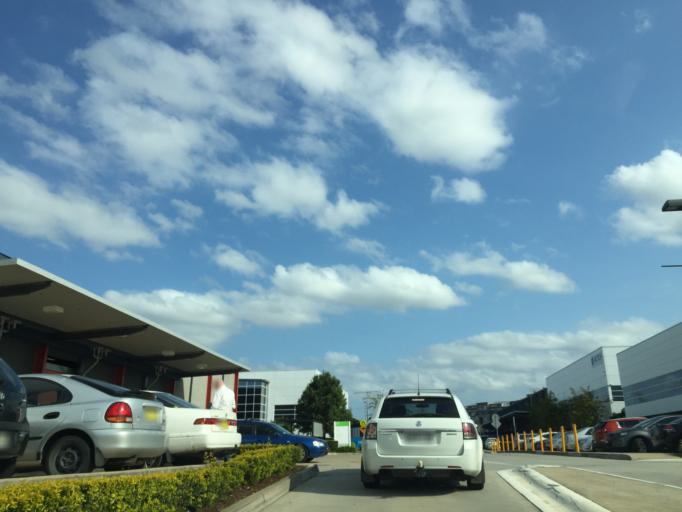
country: AU
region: New South Wales
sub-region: Strathfield
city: Homebush
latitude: -33.8589
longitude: 151.0643
